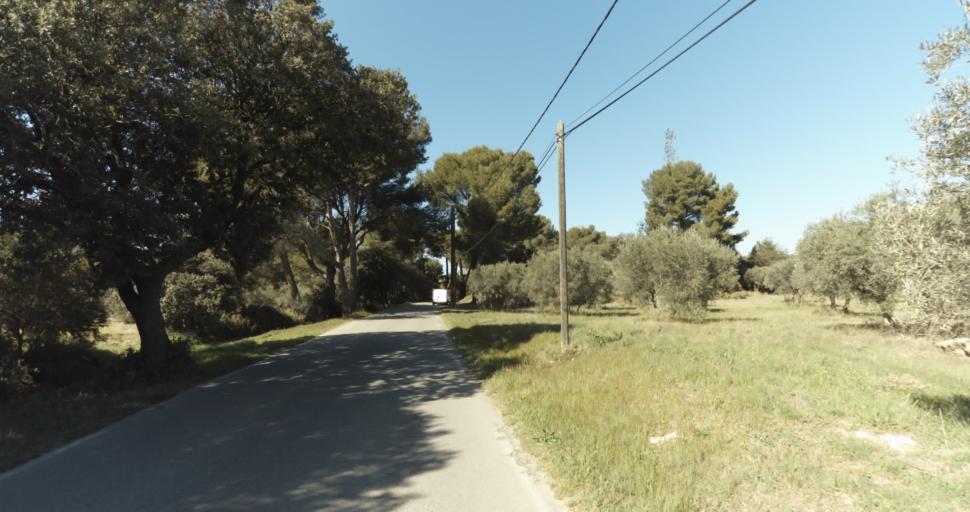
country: FR
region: Provence-Alpes-Cote d'Azur
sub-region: Departement des Bouches-du-Rhone
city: Pelissanne
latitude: 43.6432
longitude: 5.1811
